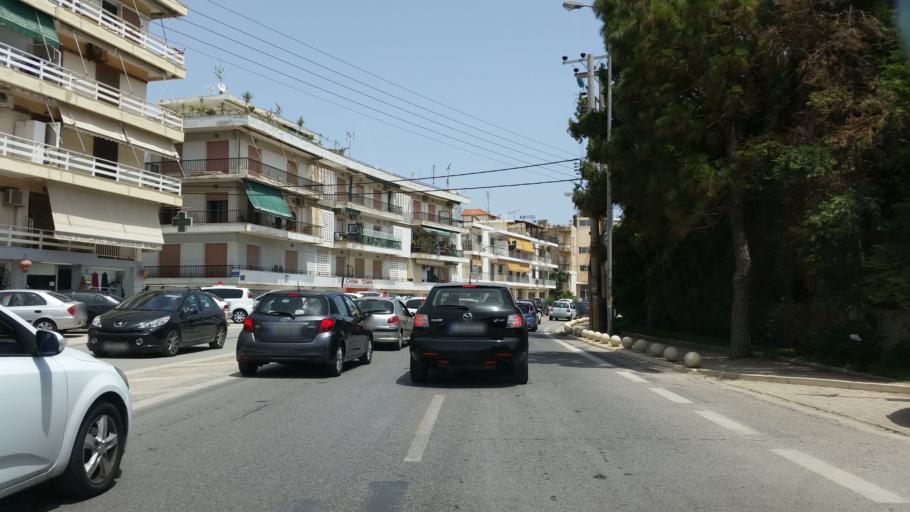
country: GR
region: Attica
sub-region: Nomarchia Anatolikis Attikis
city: Palaia Fokaia
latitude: 37.7244
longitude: 23.9443
